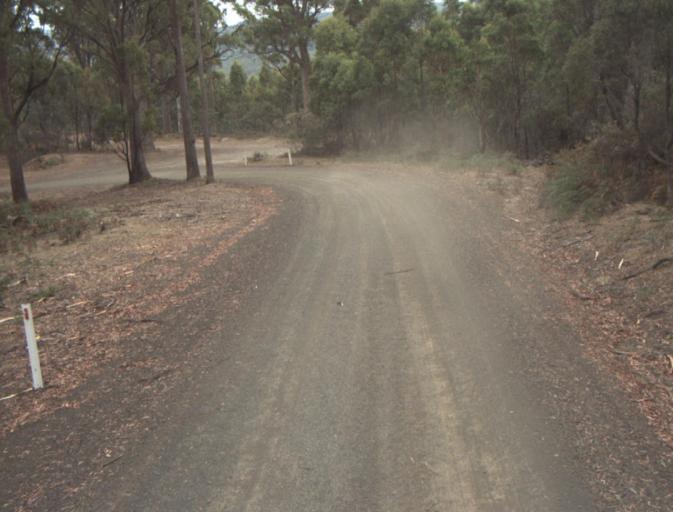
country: AU
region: Tasmania
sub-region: Northern Midlands
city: Evandale
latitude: -41.4883
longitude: 147.5452
